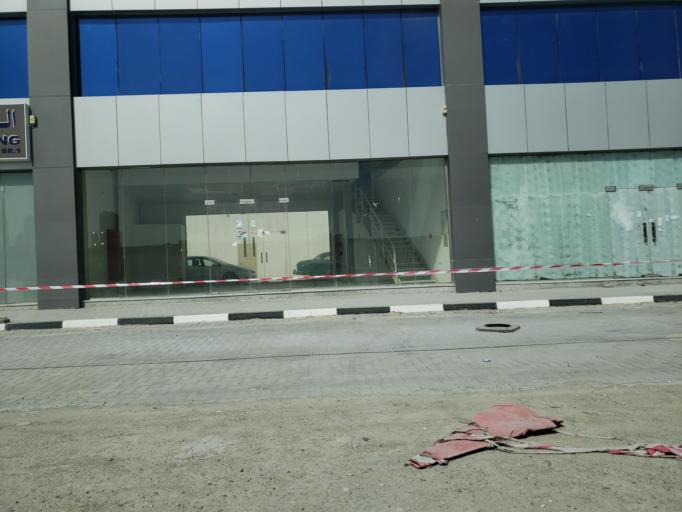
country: AE
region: Ash Shariqah
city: Sharjah
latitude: 25.3272
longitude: 55.3998
